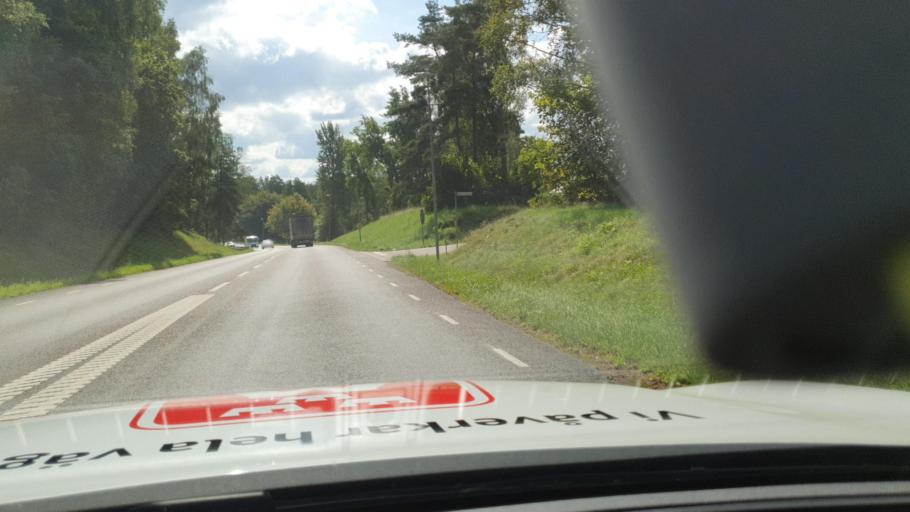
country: SE
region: Halland
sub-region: Laholms Kommun
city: Laholm
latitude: 56.4176
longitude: 13.1167
